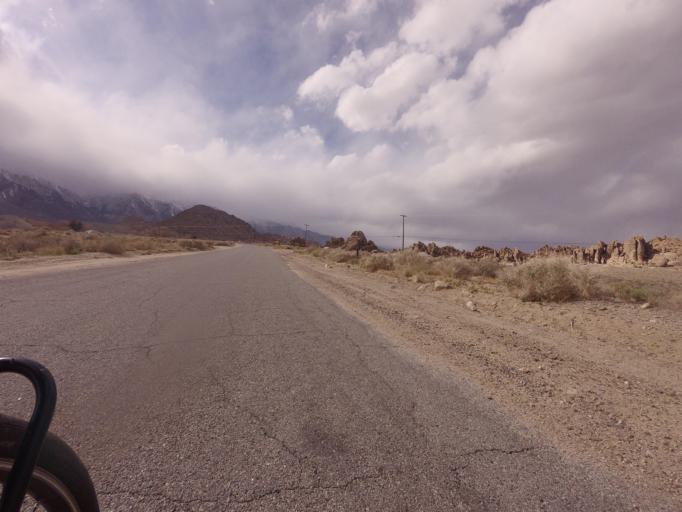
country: US
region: California
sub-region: Inyo County
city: Lone Pine
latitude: 36.5969
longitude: -118.1108
